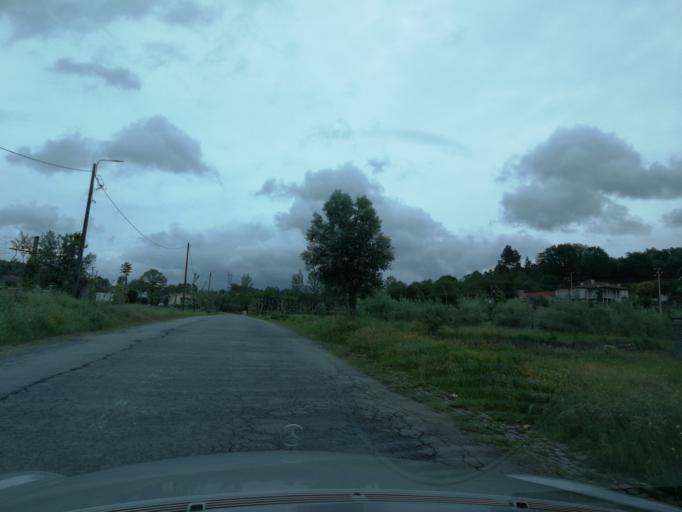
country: PT
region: Braga
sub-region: Braga
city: Adaufe
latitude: 41.6057
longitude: -8.3891
